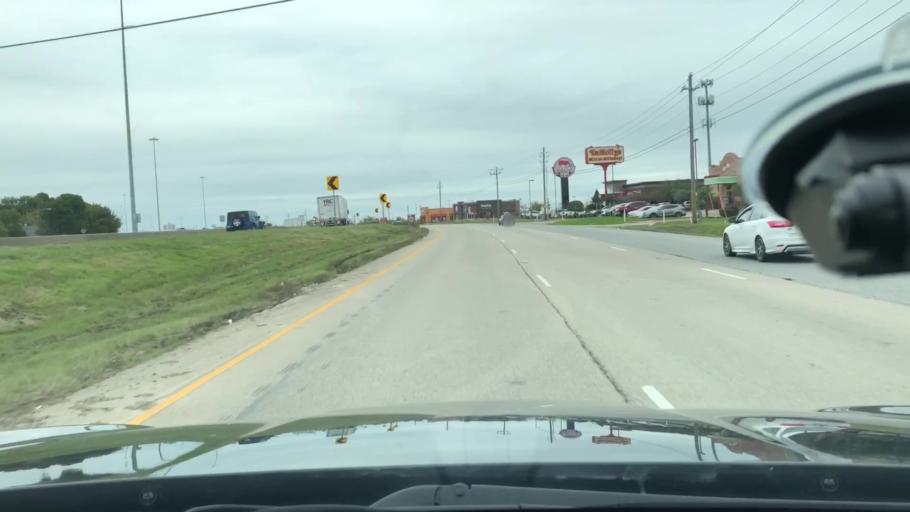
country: US
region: Texas
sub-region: Hunt County
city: Greenville
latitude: 33.0985
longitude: -96.1055
